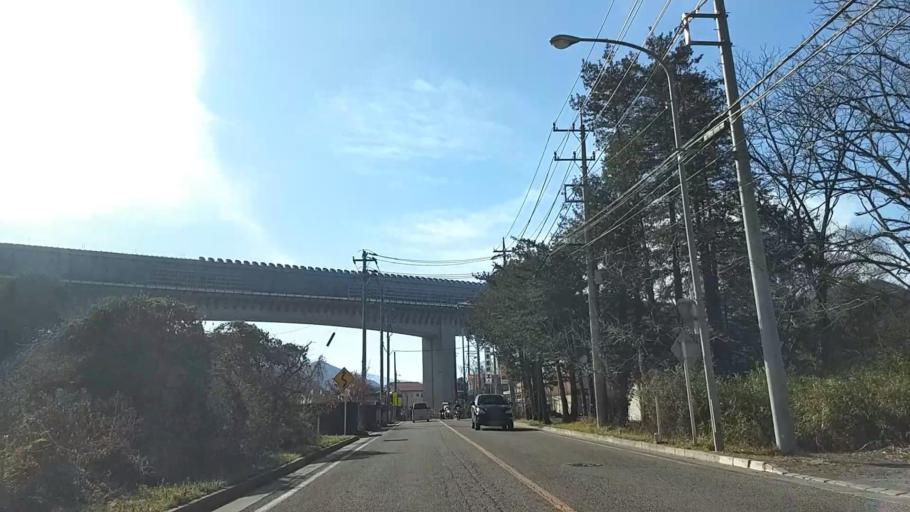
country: JP
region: Yamanashi
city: Otsuki
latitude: 35.5816
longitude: 138.9371
